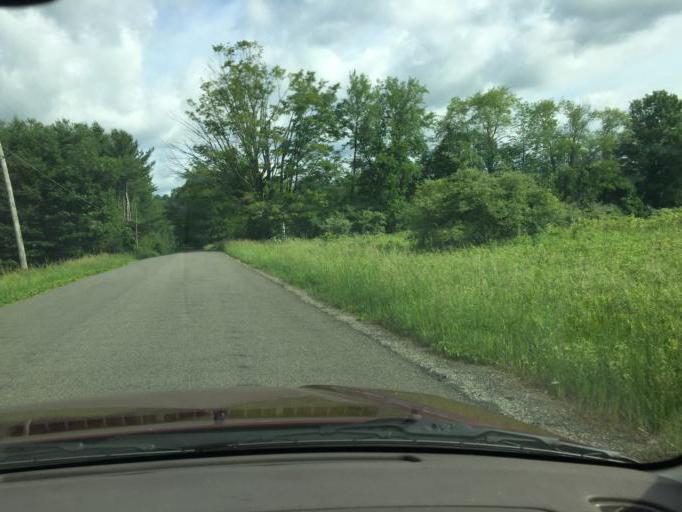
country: US
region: Connecticut
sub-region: Litchfield County
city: Litchfield
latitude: 41.8031
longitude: -73.2574
